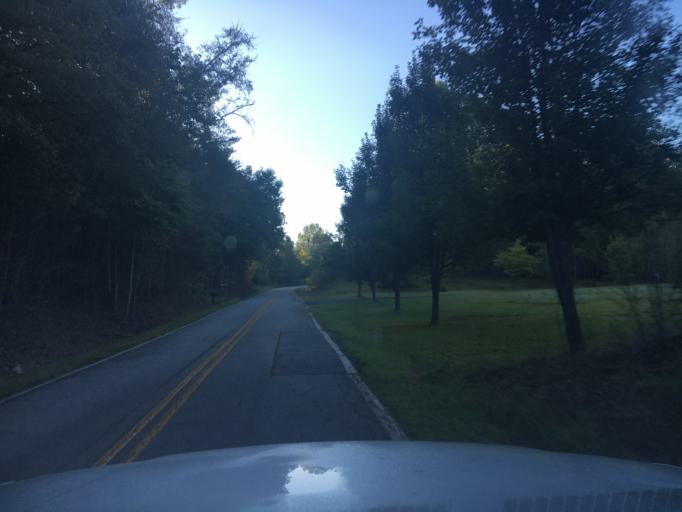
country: US
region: South Carolina
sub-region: Spartanburg County
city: Woodruff
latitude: 34.7669
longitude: -81.9625
